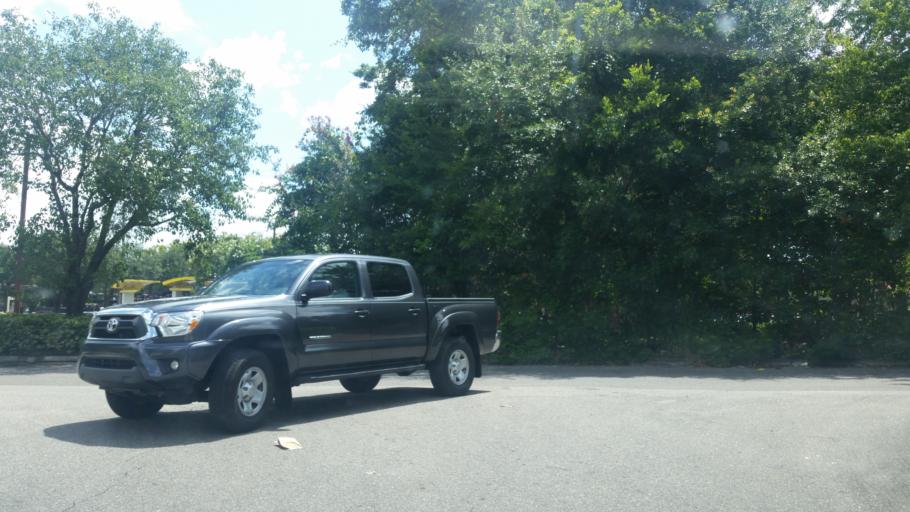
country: US
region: Florida
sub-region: Leon County
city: Tallahassee
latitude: 30.4119
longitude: -84.2819
